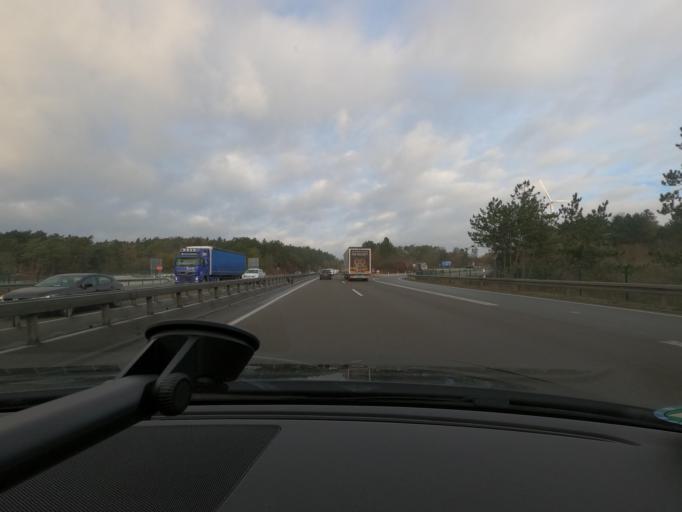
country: DE
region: Hesse
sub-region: Regierungsbezirk Kassel
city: Breuna
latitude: 51.4143
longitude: 9.1619
